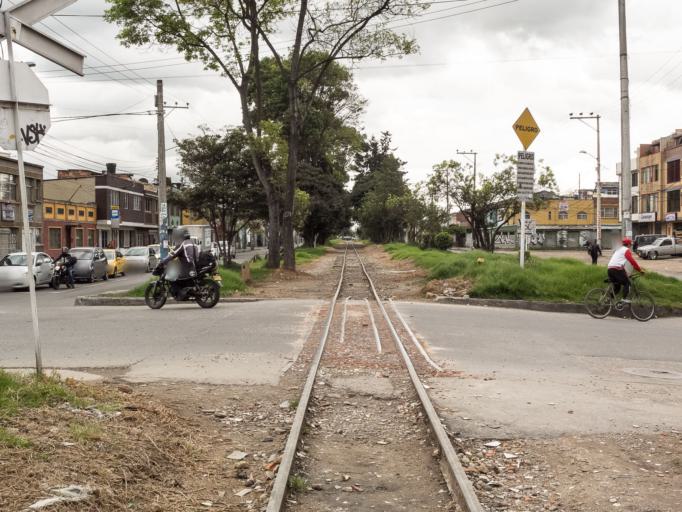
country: CO
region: Bogota D.C.
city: Bogota
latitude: 4.6719
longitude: -74.1366
